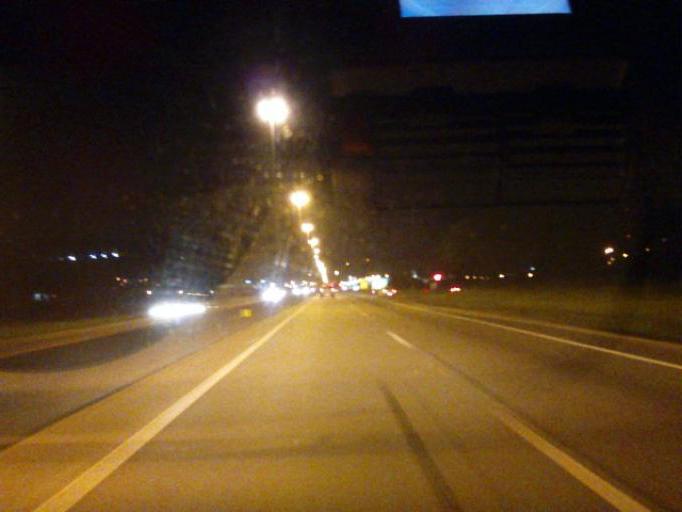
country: BR
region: Santa Catarina
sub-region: Balneario Camboriu
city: Balneario Camboriu
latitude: -27.0140
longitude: -48.6128
